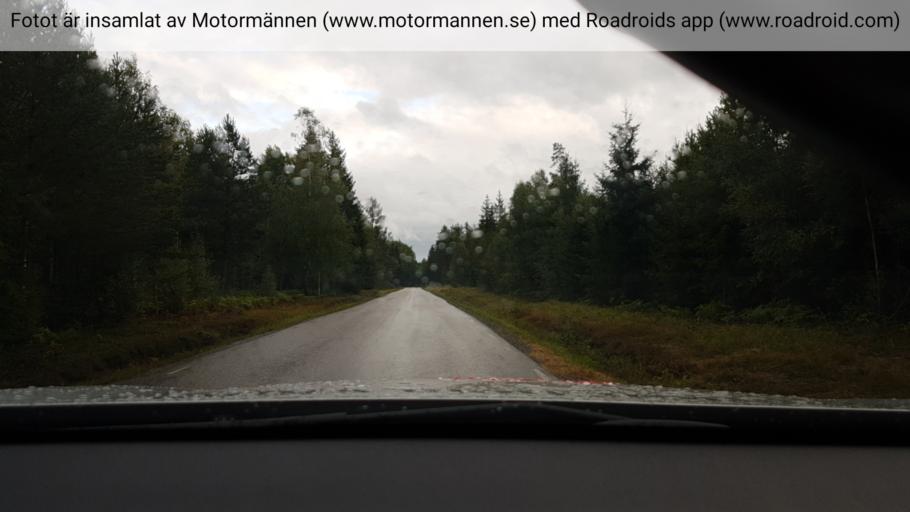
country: SE
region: Stockholm
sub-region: Haninge Kommun
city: Jordbro
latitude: 59.0847
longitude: 18.0489
